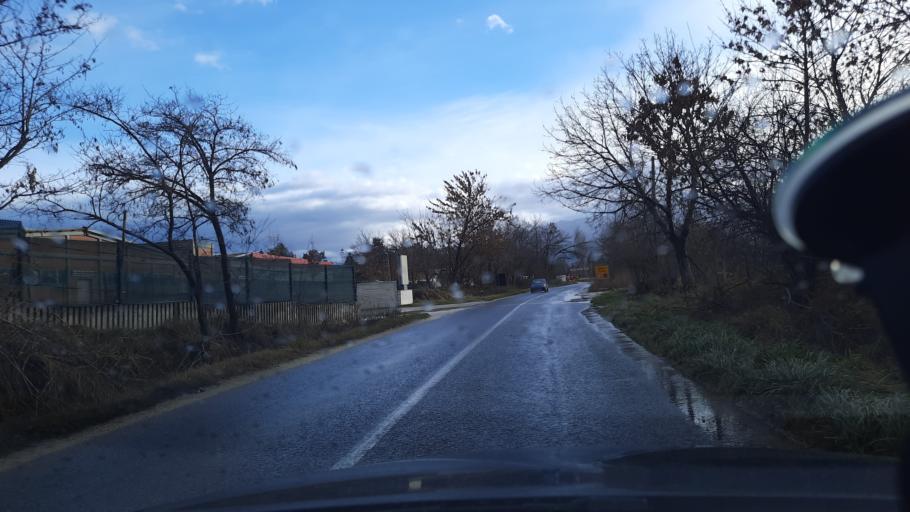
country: MK
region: Prilep
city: Markov Grad
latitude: 41.3434
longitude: 21.5181
